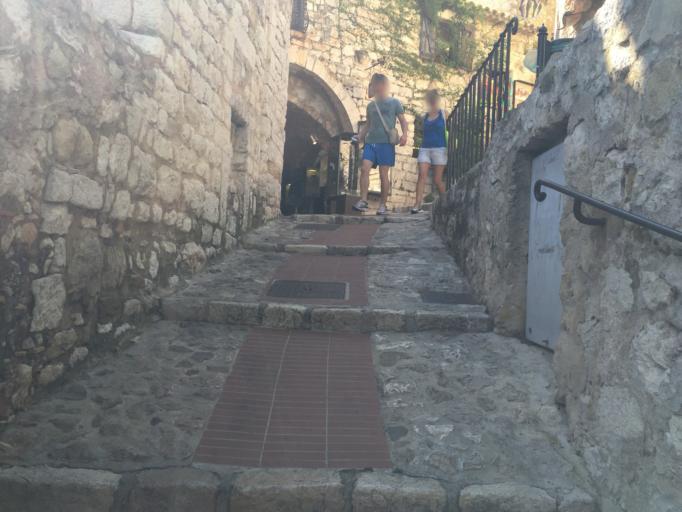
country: FR
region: Provence-Alpes-Cote d'Azur
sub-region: Departement des Alpes-Maritimes
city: Eze
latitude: 43.7277
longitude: 7.3618
